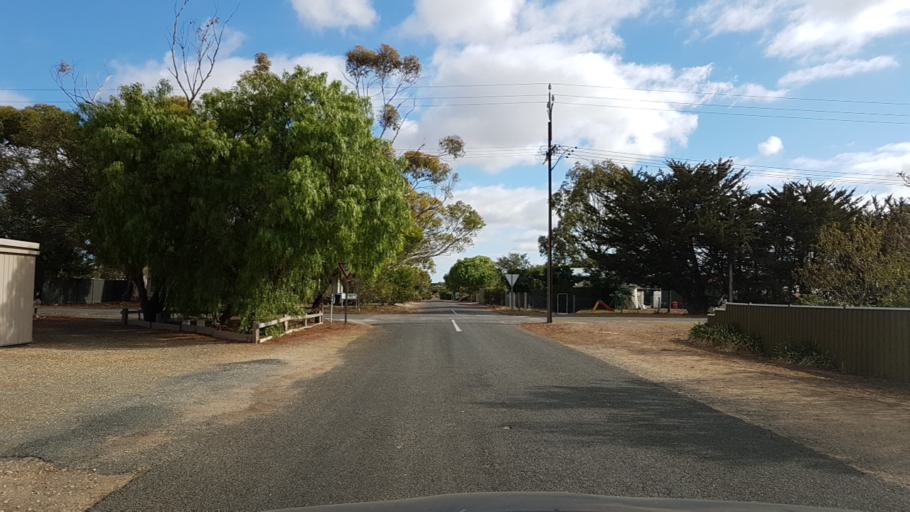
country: AU
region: South Australia
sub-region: Alexandrina
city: Langhorne Creek
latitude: -35.4043
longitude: 138.9753
